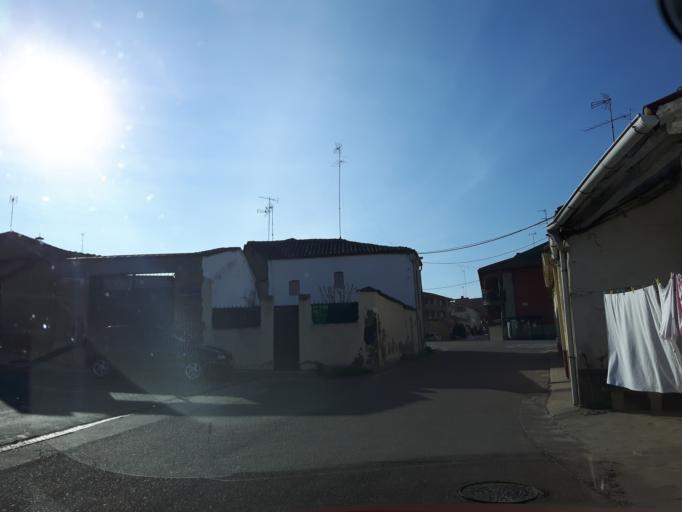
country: ES
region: Castille and Leon
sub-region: Provincia de Salamanca
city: San Cristobal de la Cuesta
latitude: 41.0292
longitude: -5.6170
